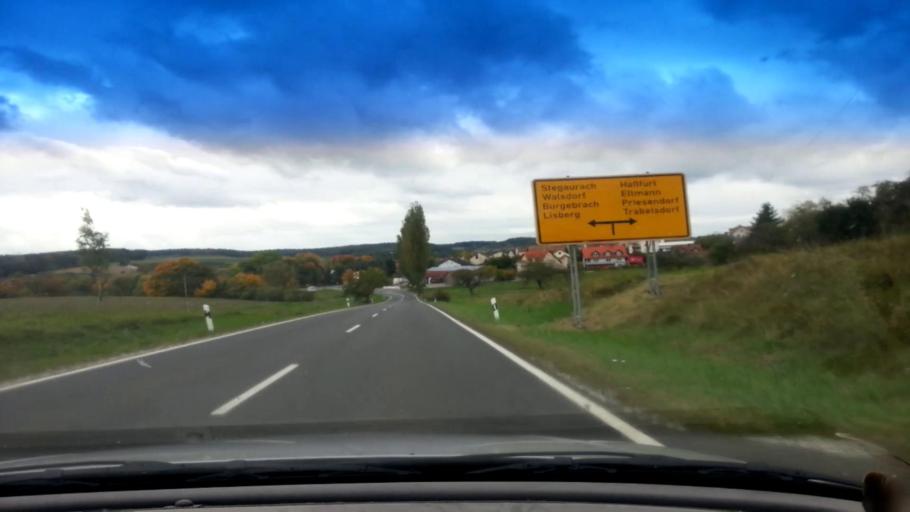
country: DE
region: Bavaria
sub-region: Upper Franconia
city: Priesendorf
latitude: 49.8949
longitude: 10.7353
